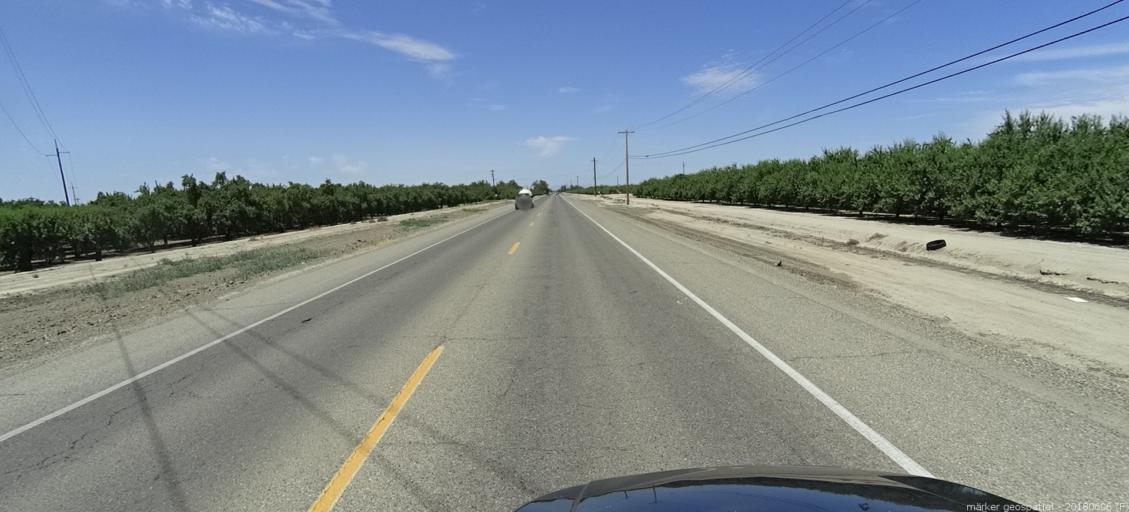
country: US
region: California
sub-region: Fresno County
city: Firebaugh
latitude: 36.8585
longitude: -120.3975
